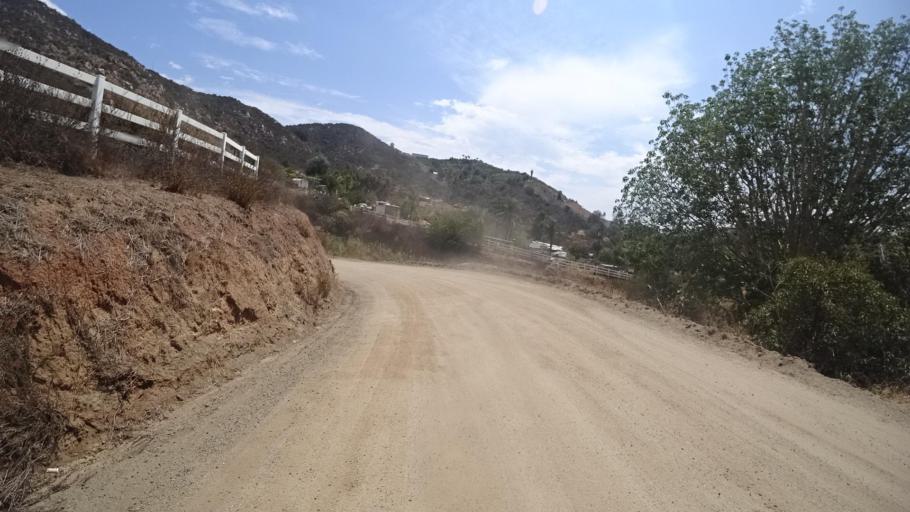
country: US
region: California
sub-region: San Diego County
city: Hidden Meadows
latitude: 33.1996
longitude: -117.0847
